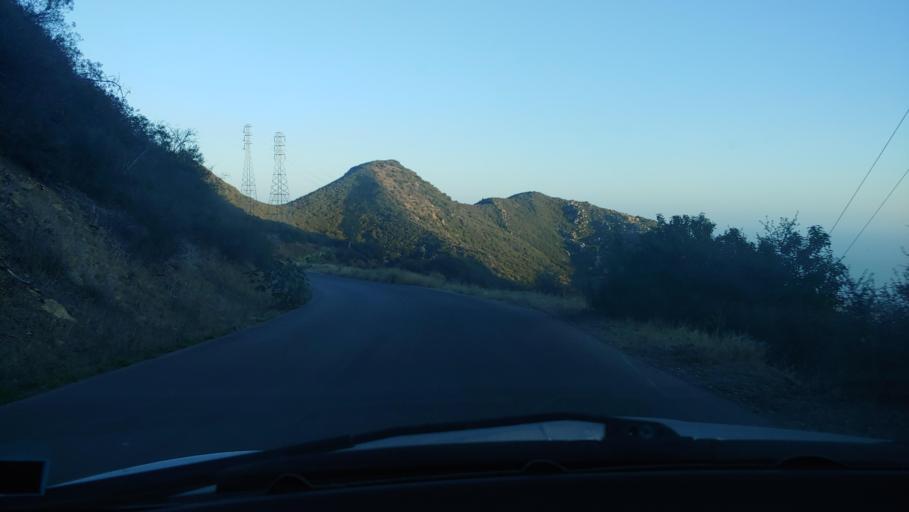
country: US
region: California
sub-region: Santa Barbara County
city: Mission Canyon
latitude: 34.4688
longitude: -119.6739
